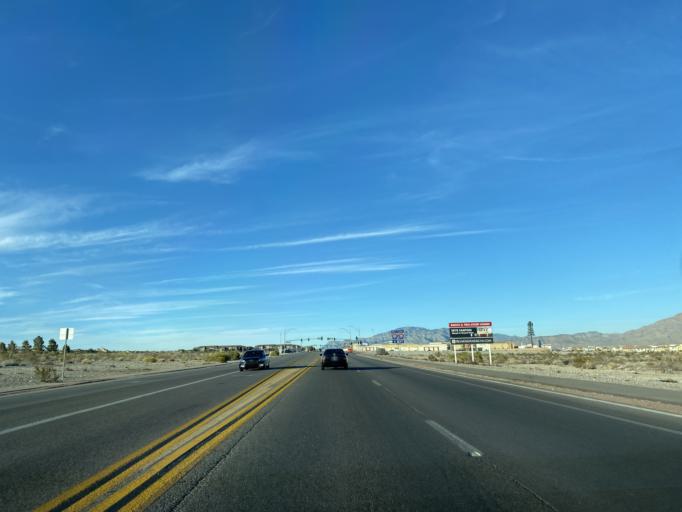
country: US
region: Nevada
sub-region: Clark County
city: Summerlin South
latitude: 36.2781
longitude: -115.3150
